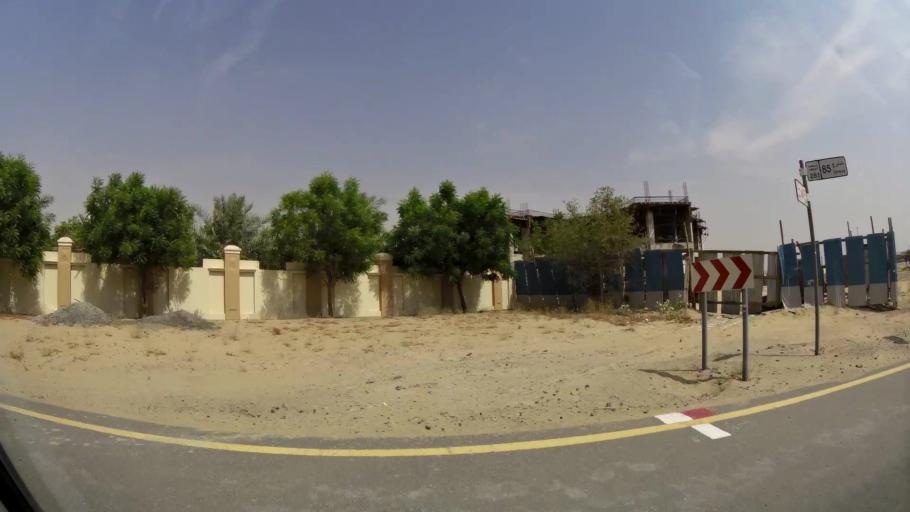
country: AE
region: Ash Shariqah
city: Sharjah
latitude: 25.2502
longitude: 55.4841
